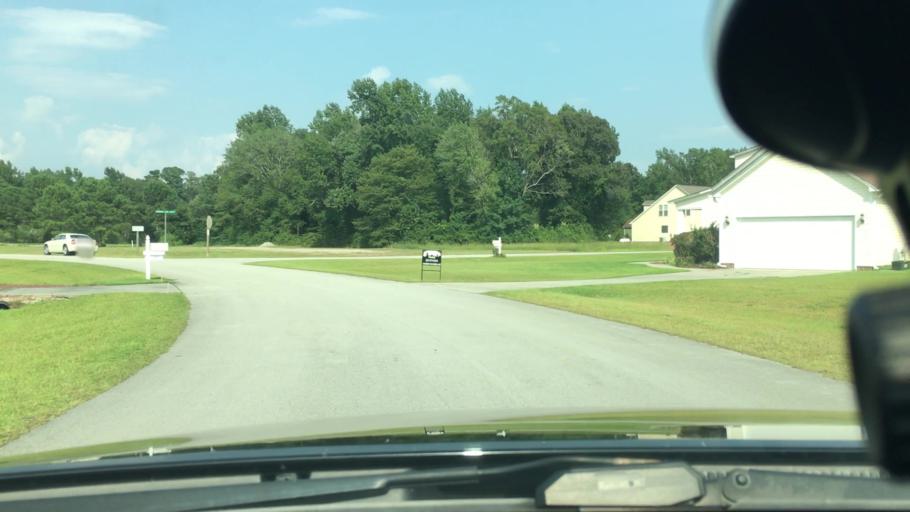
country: US
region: North Carolina
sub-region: Craven County
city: New Bern
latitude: 35.1839
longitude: -77.0543
